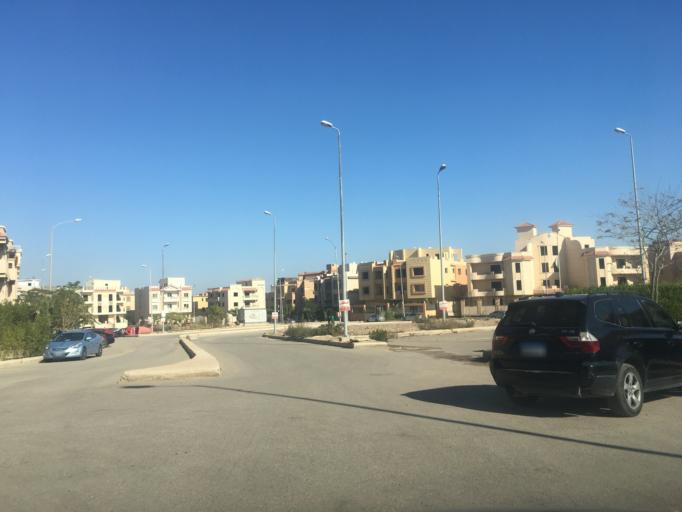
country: EG
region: Al Jizah
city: Awsim
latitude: 30.0265
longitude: 30.9841
